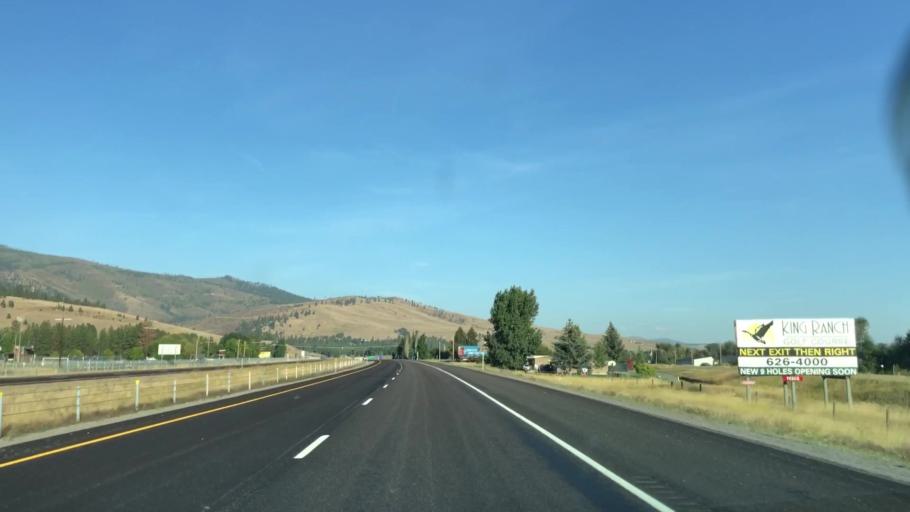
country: US
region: Montana
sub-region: Missoula County
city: Frenchtown
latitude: 47.0197
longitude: -114.2484
